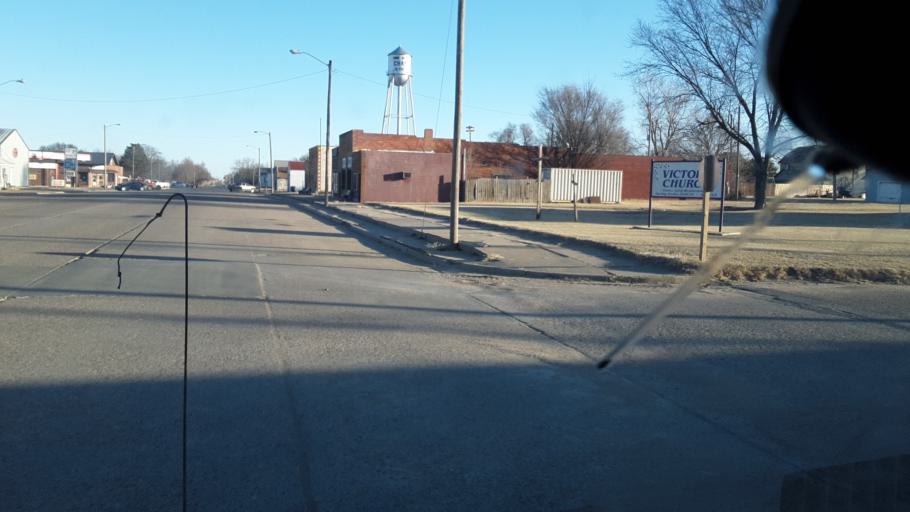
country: US
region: Kansas
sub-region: Rice County
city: Lyons
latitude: 38.3531
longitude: -98.3494
